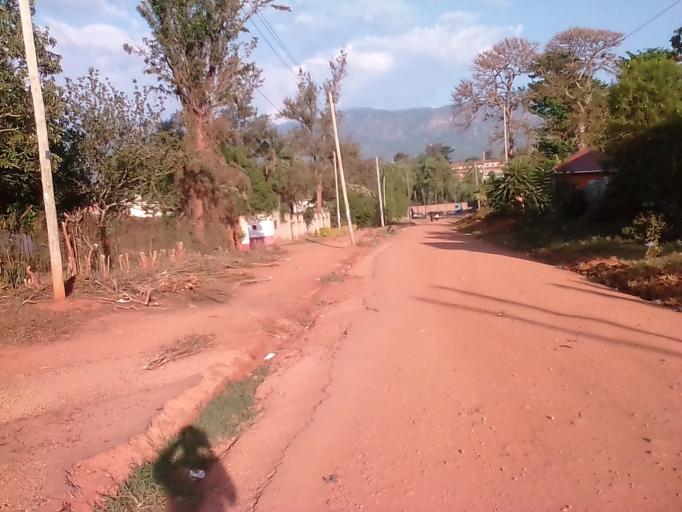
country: UG
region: Eastern Region
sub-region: Mbale District
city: Mbale
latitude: 1.0871
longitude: 34.1760
